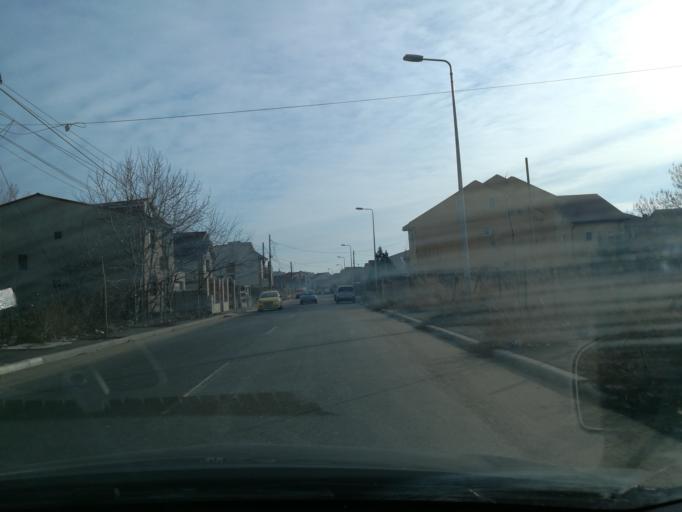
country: RO
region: Constanta
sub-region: Municipiul Constanta
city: Constanta
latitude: 44.1828
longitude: 28.6115
